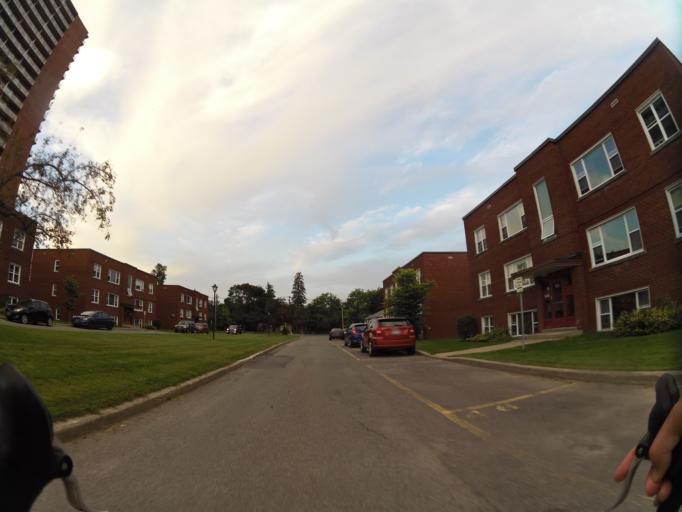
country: CA
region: Ontario
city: Ottawa
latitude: 45.3864
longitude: -75.7429
